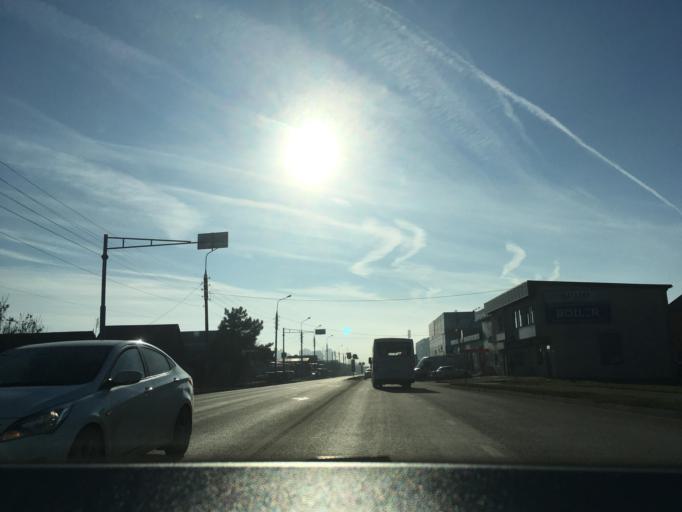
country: RU
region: Krasnodarskiy
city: Krasnodar
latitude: 45.1198
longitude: 39.0114
